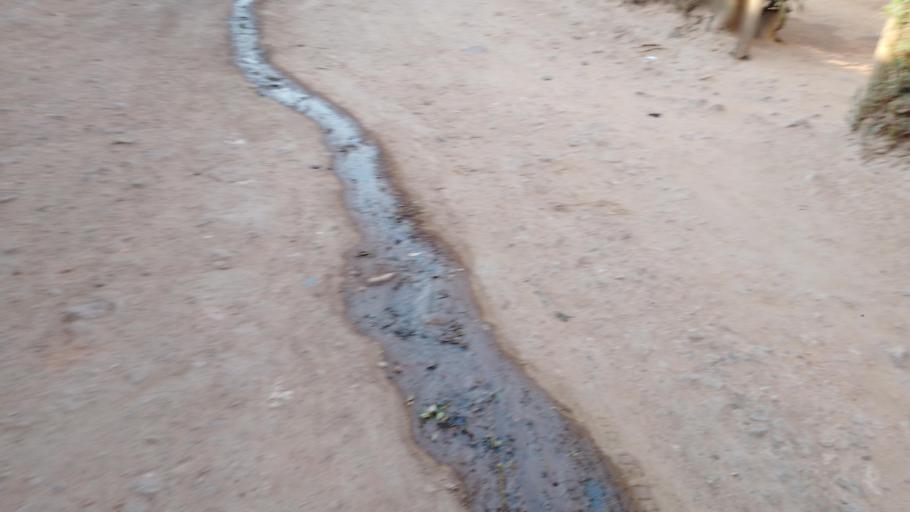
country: ZM
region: Lusaka
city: Lusaka
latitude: -15.3990
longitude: 28.3701
